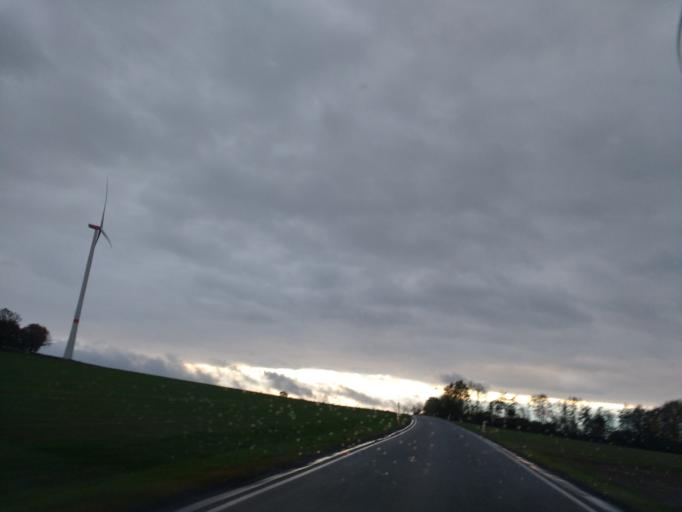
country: DE
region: Hesse
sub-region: Regierungsbezirk Kassel
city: Martinhagen
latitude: 51.3013
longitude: 9.3048
